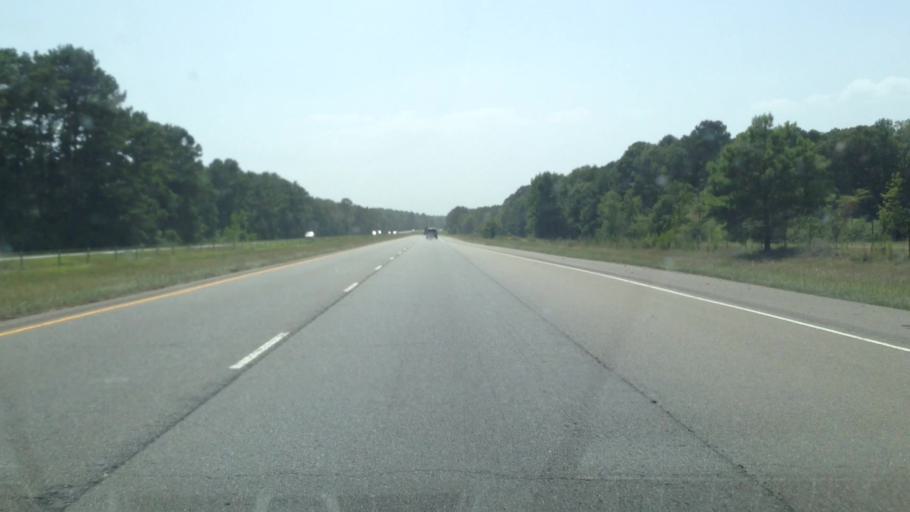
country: US
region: Louisiana
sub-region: Bossier Parish
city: Haughton
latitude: 32.5784
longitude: -93.4385
